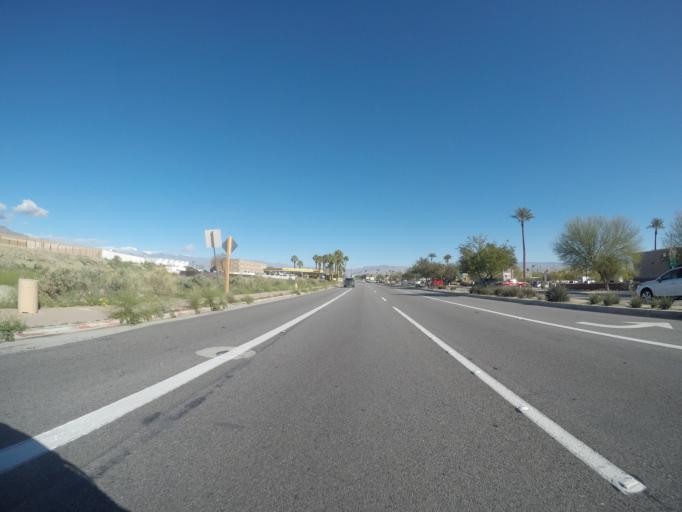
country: US
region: California
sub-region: Riverside County
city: Cathedral City
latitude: 33.8141
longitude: -116.4930
